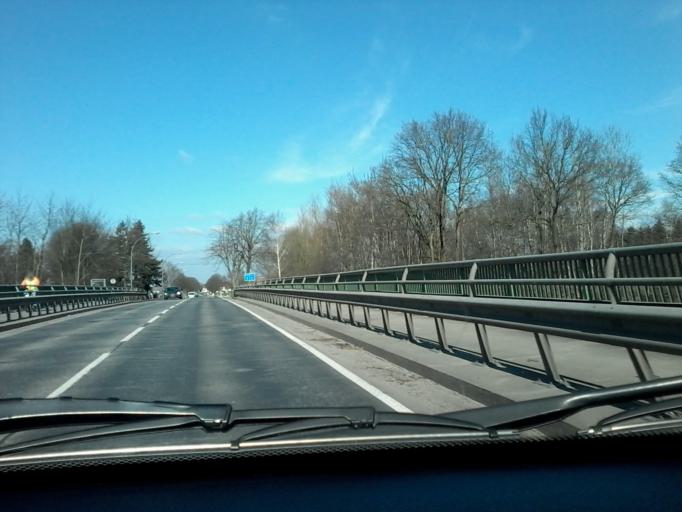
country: DE
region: Lower Saxony
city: Achim
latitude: 53.0236
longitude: 9.0316
